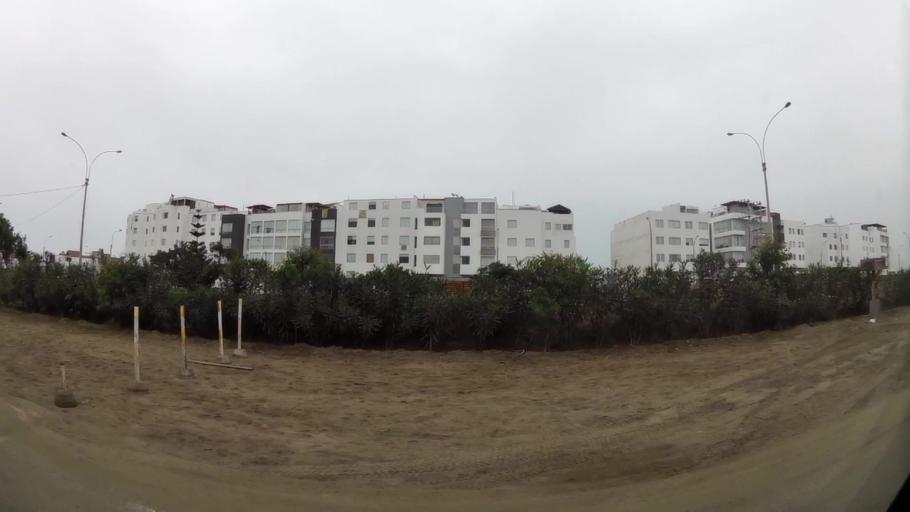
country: PE
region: Lima
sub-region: Lima
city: Punta Hermosa
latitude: -12.3313
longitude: -76.8292
